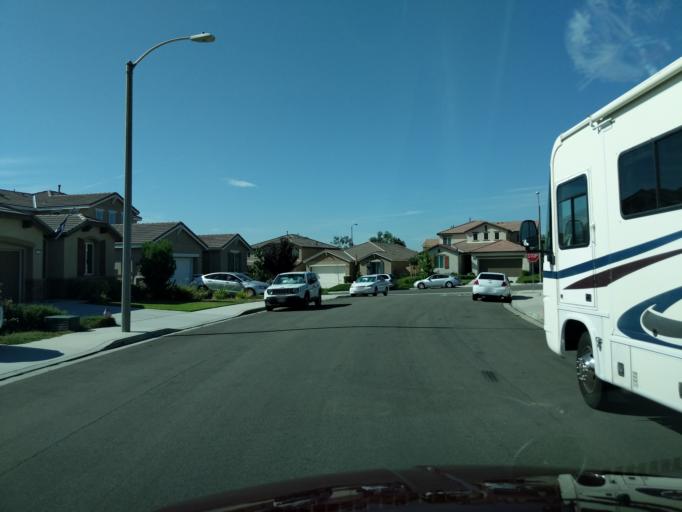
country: US
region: California
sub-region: San Bernardino County
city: Muscoy
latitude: 34.1858
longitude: -117.4163
